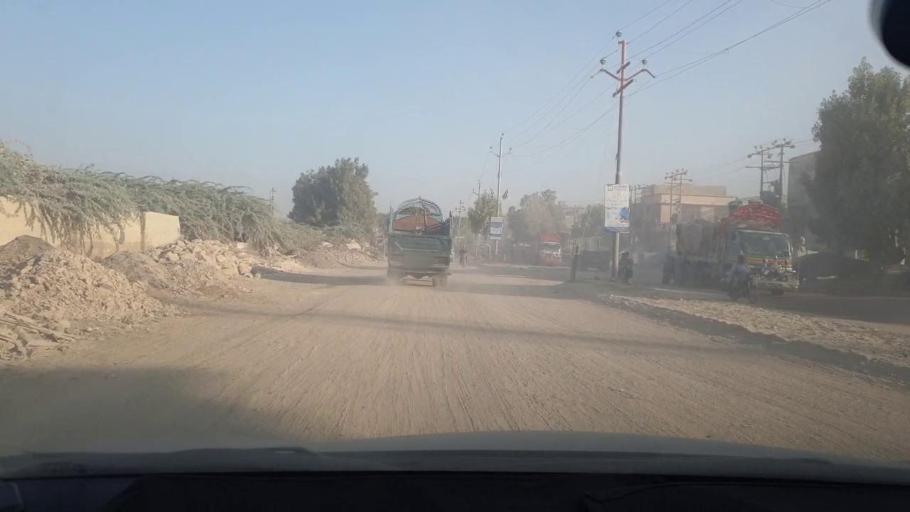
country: PK
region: Sindh
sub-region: Karachi District
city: Karachi
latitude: 24.9731
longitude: 67.0398
